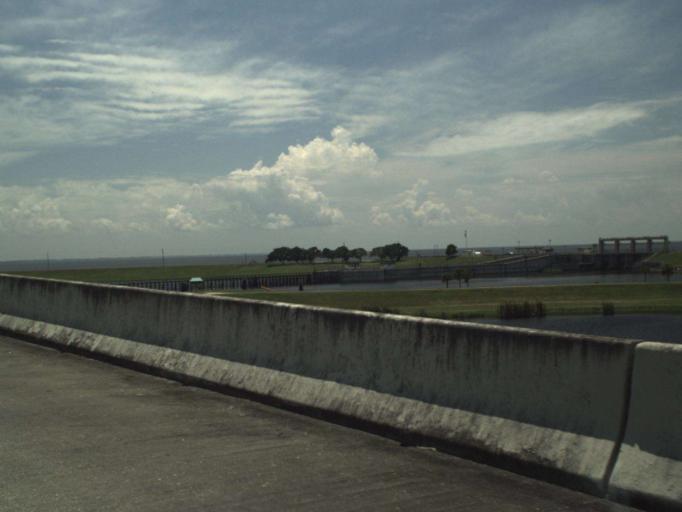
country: US
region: Florida
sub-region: Martin County
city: Indiantown
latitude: 26.9884
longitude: -80.6180
